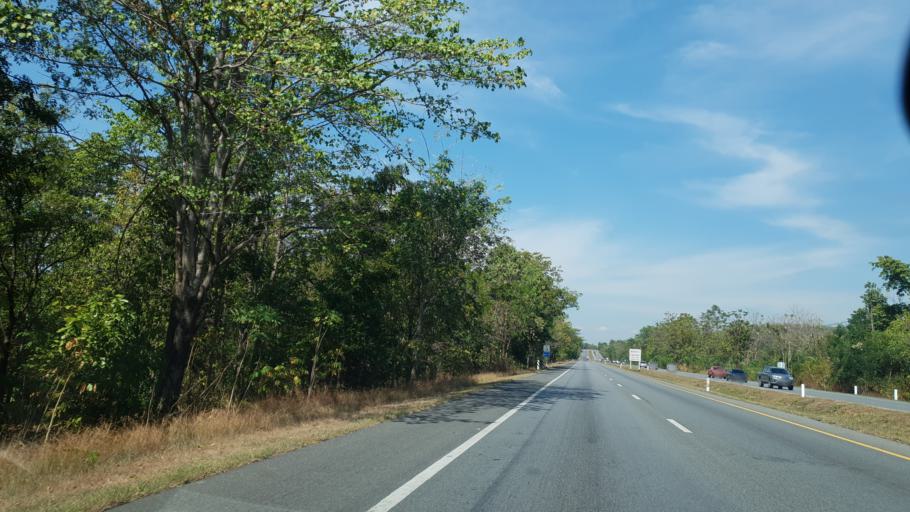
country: TH
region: Uttaradit
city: Thong Saen Khan
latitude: 17.4106
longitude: 100.2289
